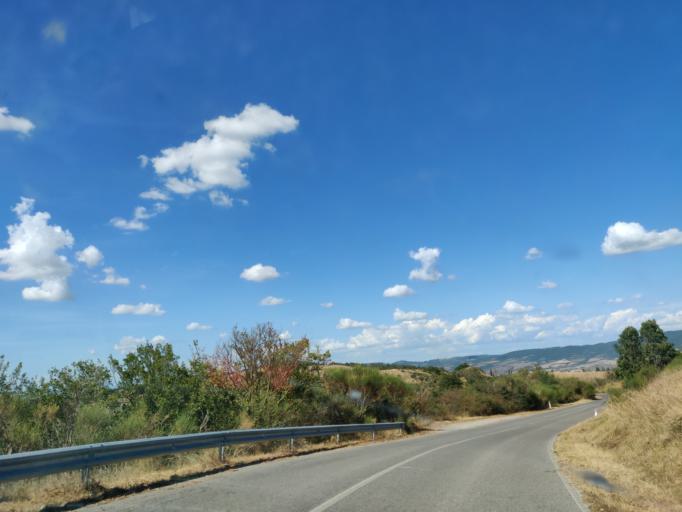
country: IT
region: Tuscany
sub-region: Provincia di Siena
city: Radicofani
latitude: 42.9364
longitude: 11.7325
